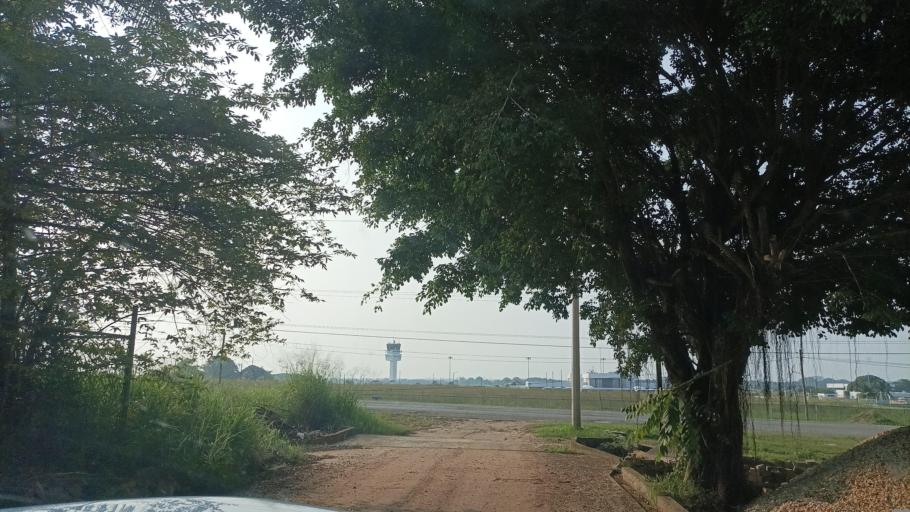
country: MX
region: Veracruz
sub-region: Cosoleacaque
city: Residencial las Olas
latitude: 18.1008
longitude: -94.5740
